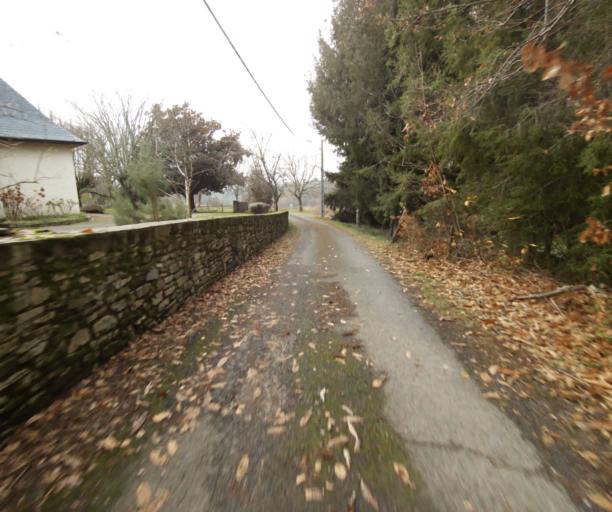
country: FR
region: Limousin
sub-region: Departement de la Correze
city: Chameyrat
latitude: 45.2329
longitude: 1.7029
